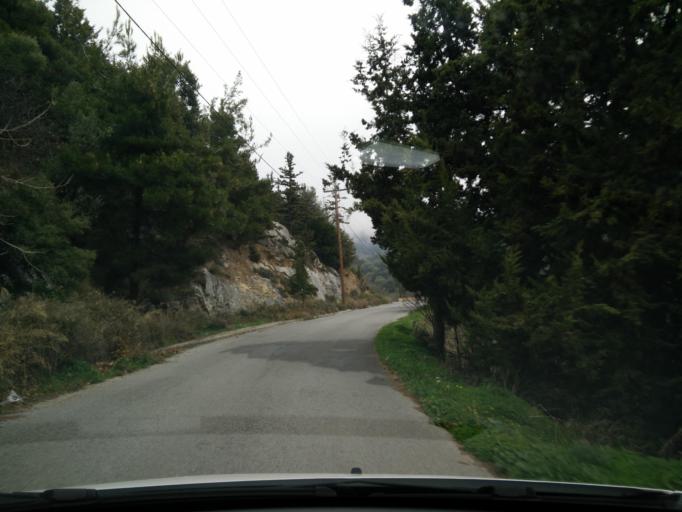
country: GR
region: Crete
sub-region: Nomos Lasithiou
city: Kritsa
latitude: 35.0442
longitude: 25.4870
